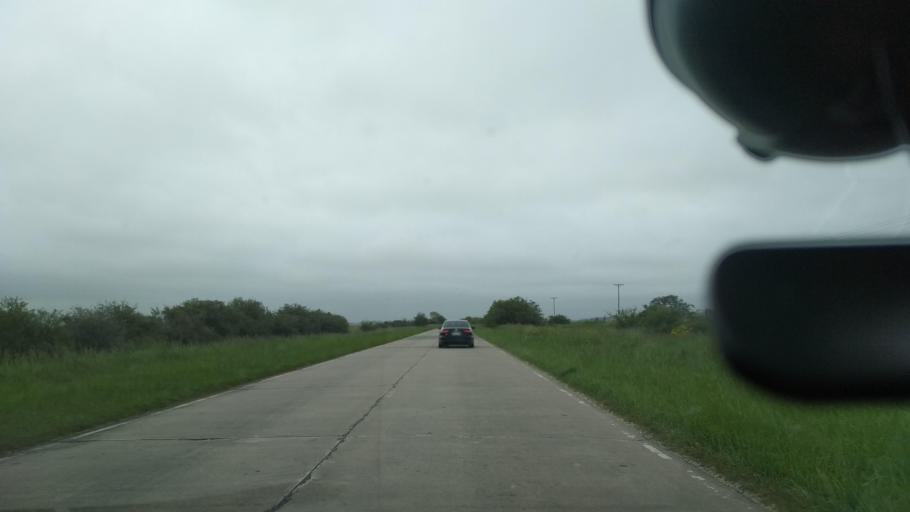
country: AR
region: Buenos Aires
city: Veronica
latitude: -35.5754
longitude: -57.2814
